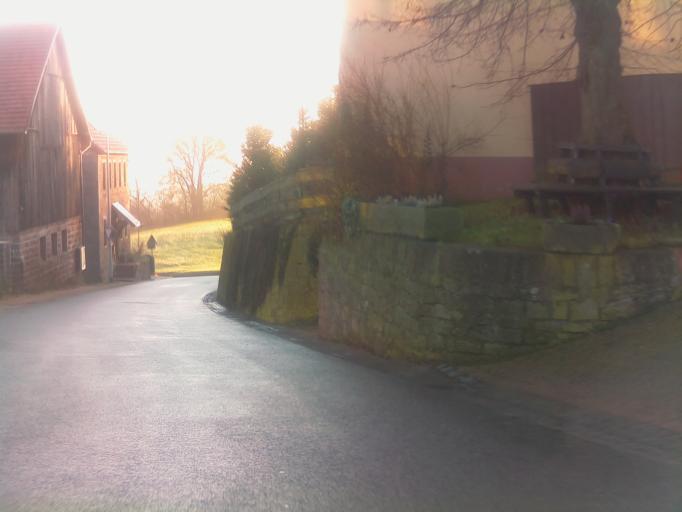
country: DE
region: Bavaria
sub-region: Regierungsbezirk Unterfranken
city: Eichenbuhl
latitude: 49.6653
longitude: 9.3572
